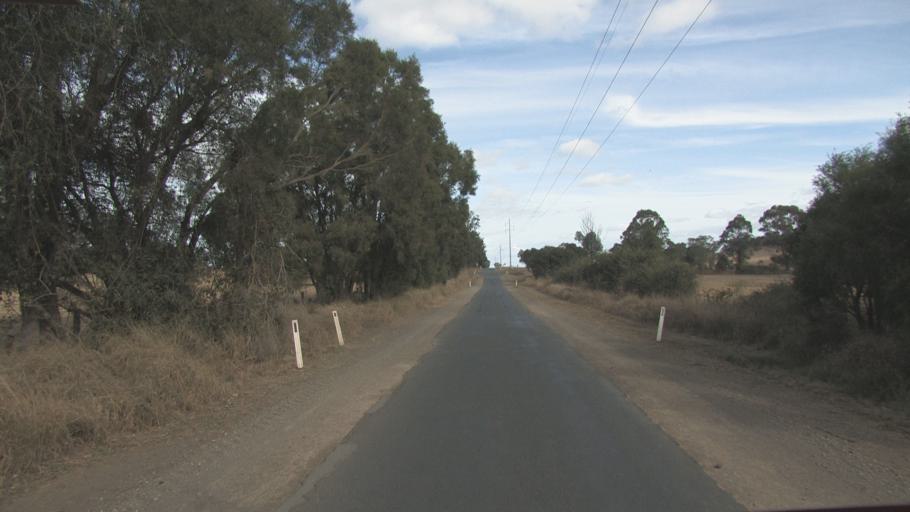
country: AU
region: Queensland
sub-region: Logan
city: Cedar Vale
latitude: -27.9189
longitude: 153.0130
